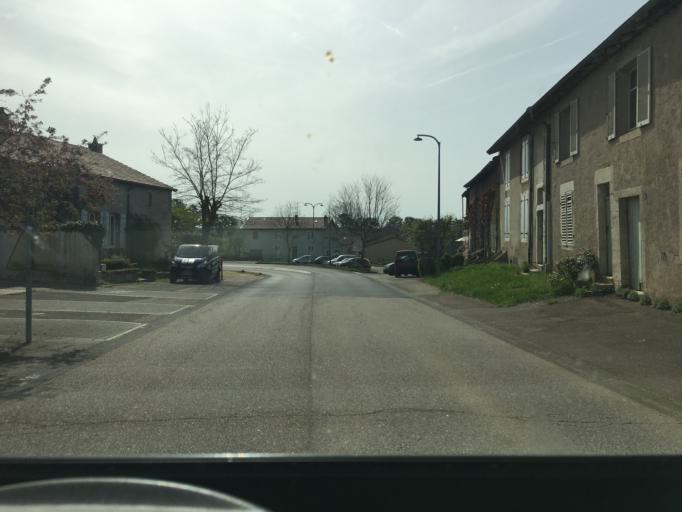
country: FR
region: Lorraine
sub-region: Departement de Meurthe-et-Moselle
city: Gondreville
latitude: 48.6590
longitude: 5.9774
